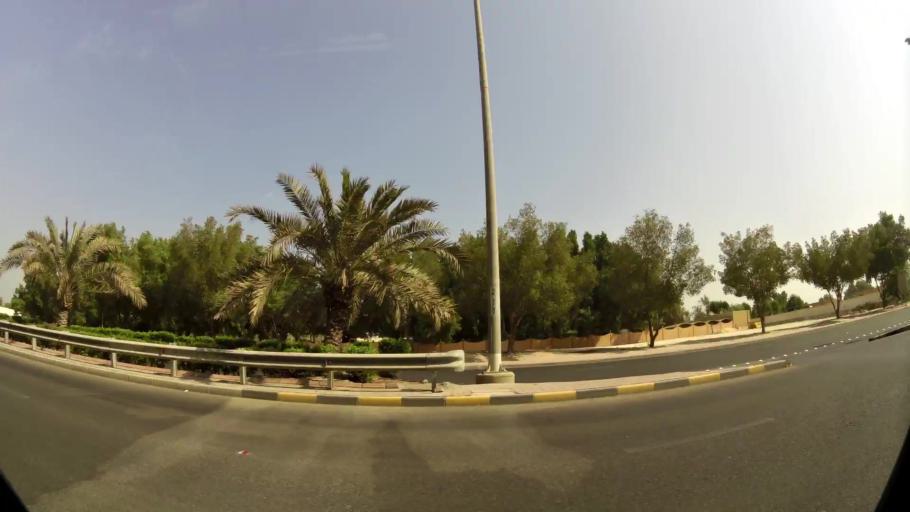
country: KW
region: Al Ahmadi
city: Al Fintas
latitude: 29.1833
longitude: 48.1181
